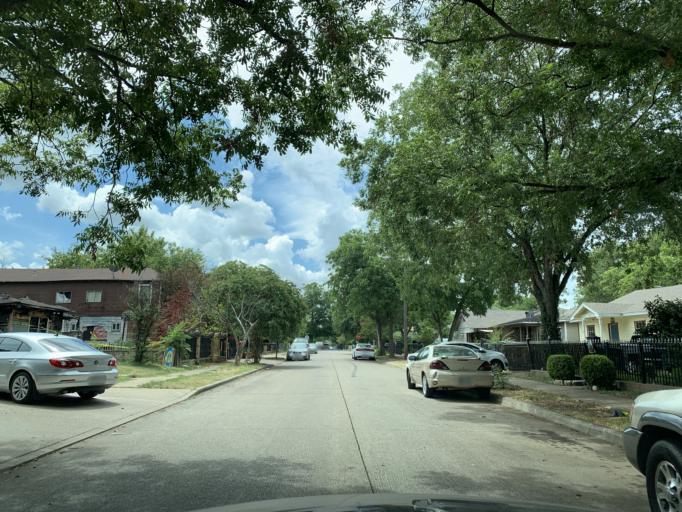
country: US
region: Texas
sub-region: Dallas County
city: Cockrell Hill
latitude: 32.7525
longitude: -96.8713
